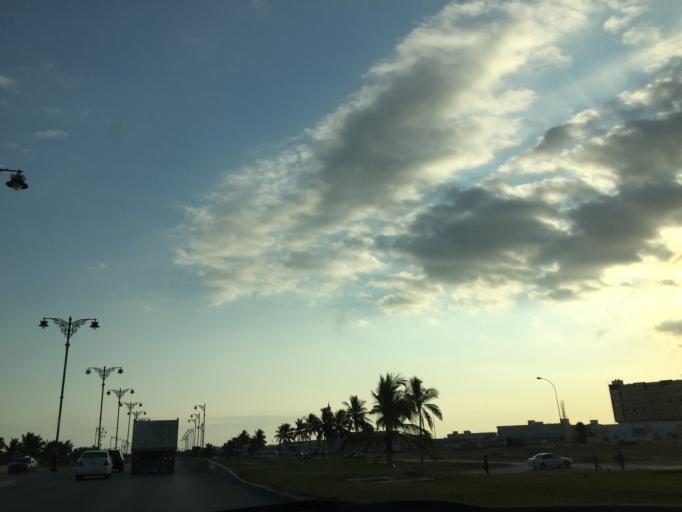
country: OM
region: Zufar
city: Salalah
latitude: 17.0260
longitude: 54.0582
